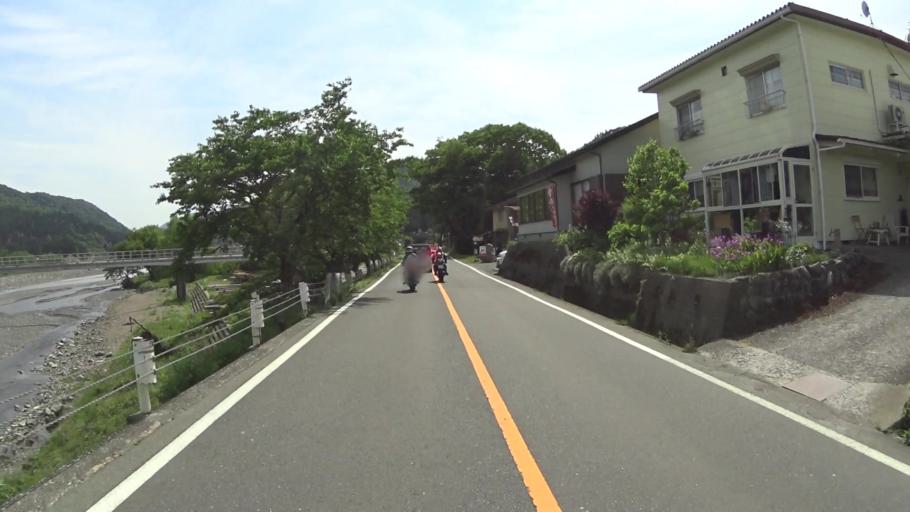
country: JP
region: Shiga Prefecture
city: Kitahama
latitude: 35.3465
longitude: 135.9117
